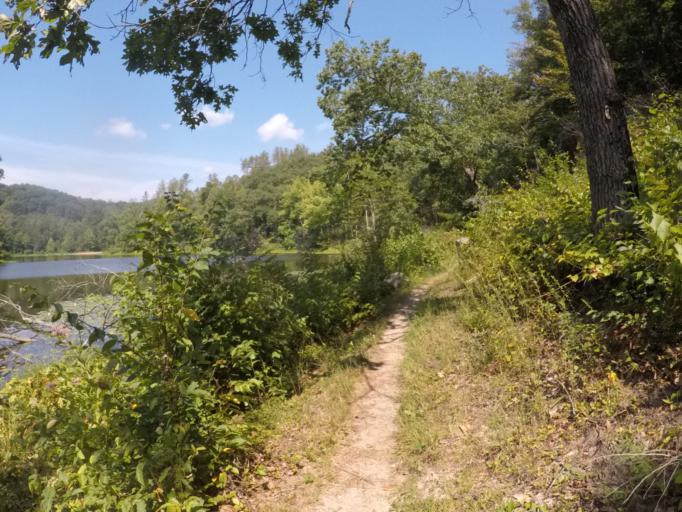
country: US
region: Ohio
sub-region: Lawrence County
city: Ironton
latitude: 38.6186
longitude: -82.6245
